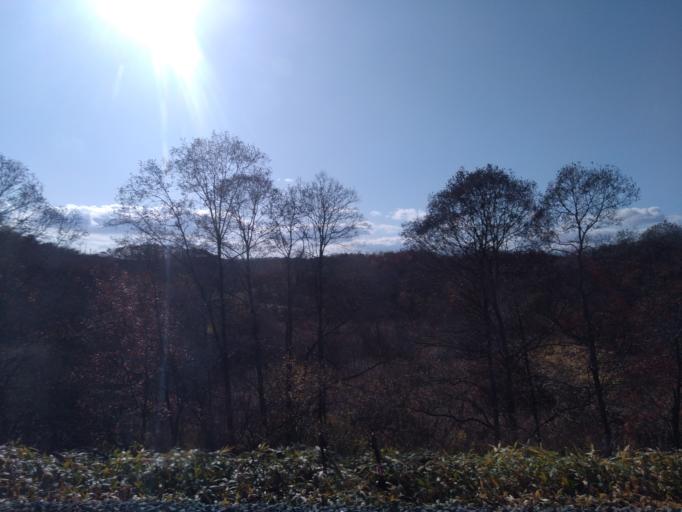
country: JP
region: Hokkaido
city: Chitose
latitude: 42.7822
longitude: 141.7058
